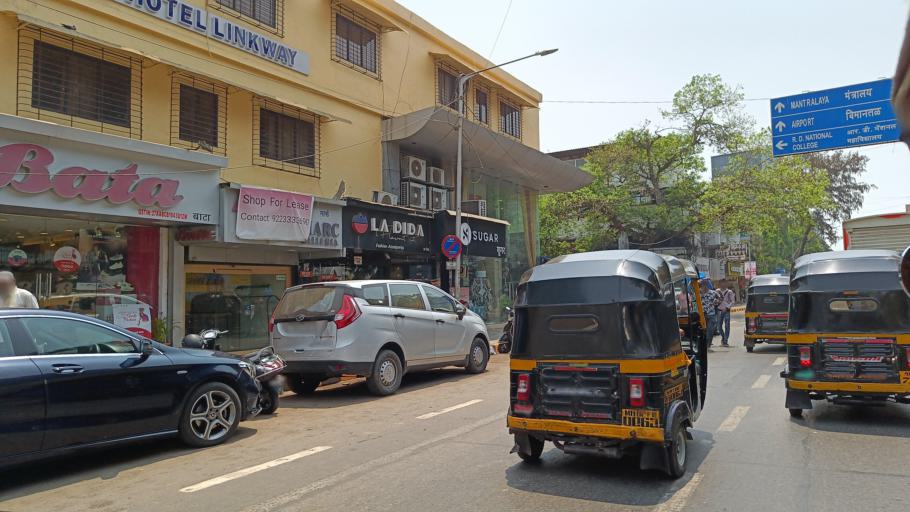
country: IN
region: Maharashtra
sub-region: Mumbai Suburban
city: Mumbai
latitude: 19.0651
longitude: 72.8346
